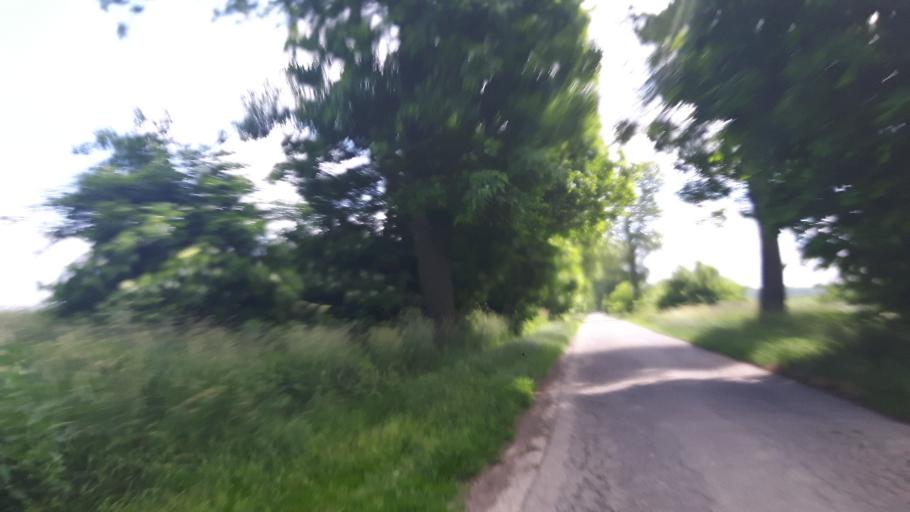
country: PL
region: West Pomeranian Voivodeship
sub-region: Powiat slawienski
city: Darlowo
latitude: 54.4699
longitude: 16.4789
